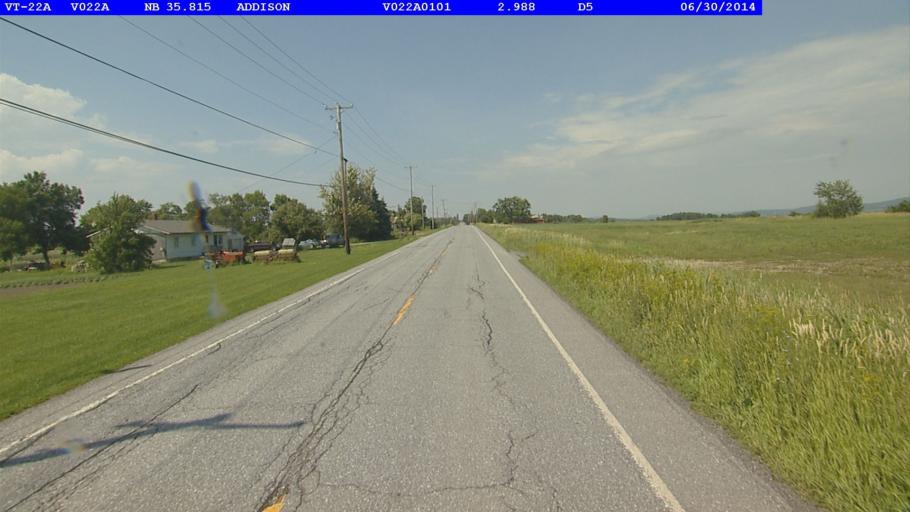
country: US
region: Vermont
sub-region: Addison County
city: Vergennes
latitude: 44.0725
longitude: -73.3040
